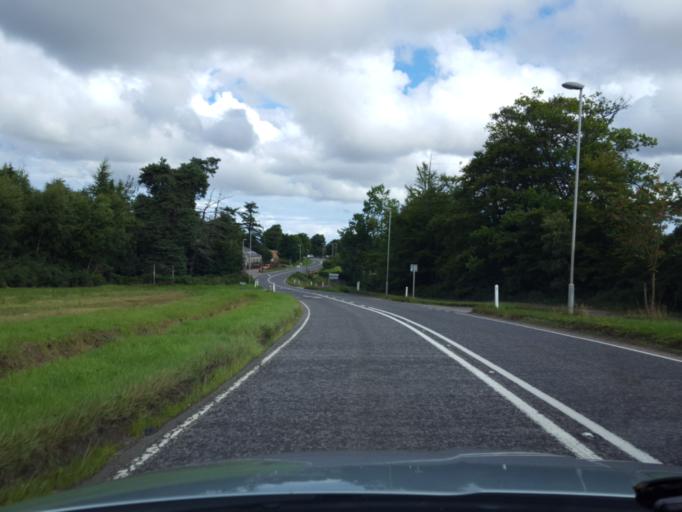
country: GB
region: Scotland
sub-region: Moray
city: Lhanbryd
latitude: 57.5935
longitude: -3.2800
